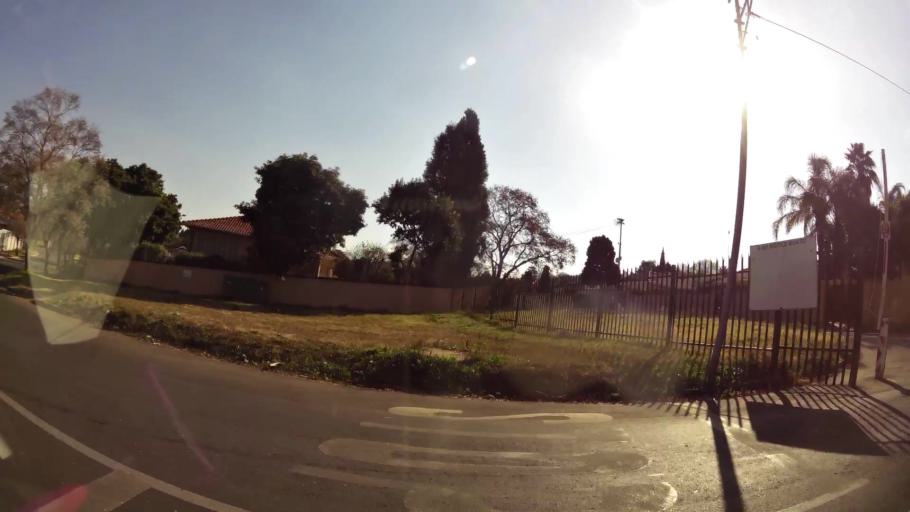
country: ZA
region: Gauteng
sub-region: City of Johannesburg Metropolitan Municipality
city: Johannesburg
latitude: -26.1746
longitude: 28.1053
